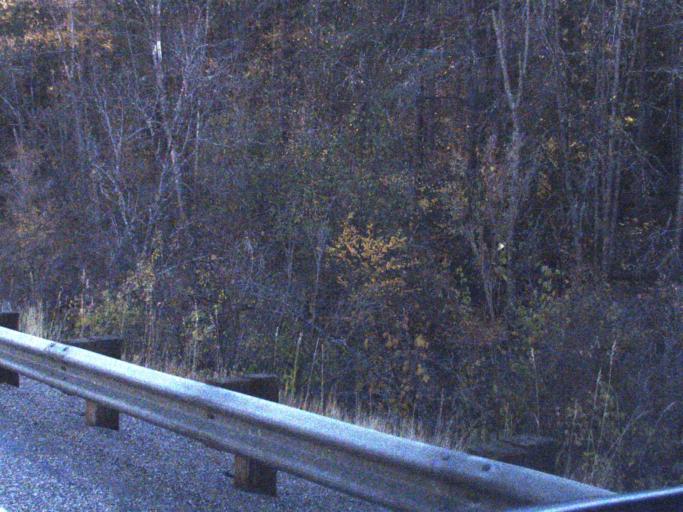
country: US
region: Washington
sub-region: Stevens County
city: Kettle Falls
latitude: 48.5863
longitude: -118.1971
